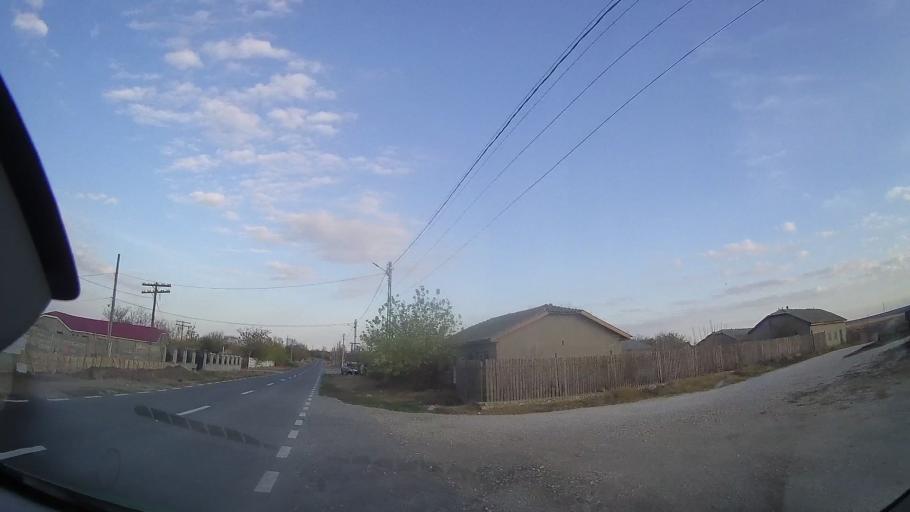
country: RO
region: Constanta
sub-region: Comuna Chirnogeni
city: Plopeni
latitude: 43.9508
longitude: 28.1823
